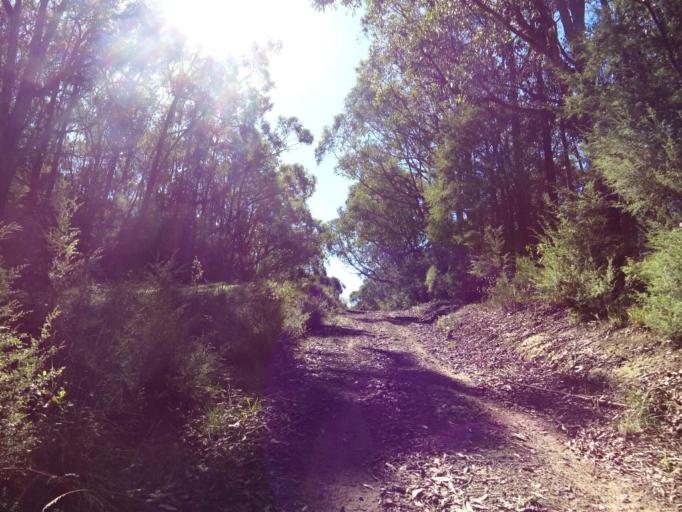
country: AU
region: Victoria
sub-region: Yarra Ranges
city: Woori Yallock
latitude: -37.7452
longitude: 145.5529
